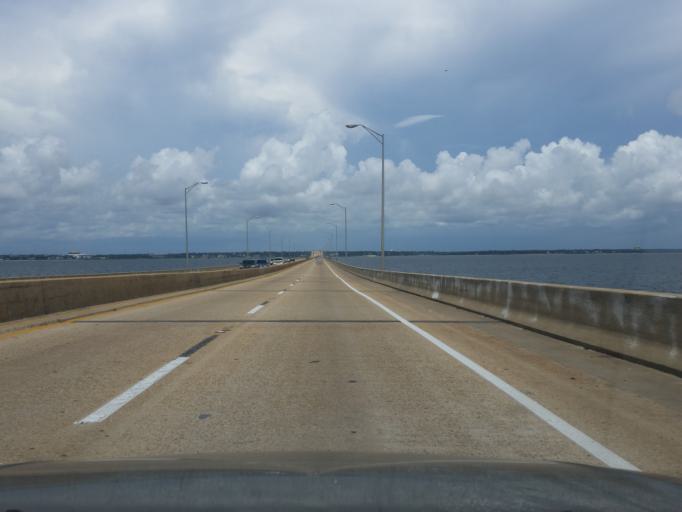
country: US
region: Florida
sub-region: Santa Rosa County
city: Gulf Breeze
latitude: 30.3809
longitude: -87.1799
